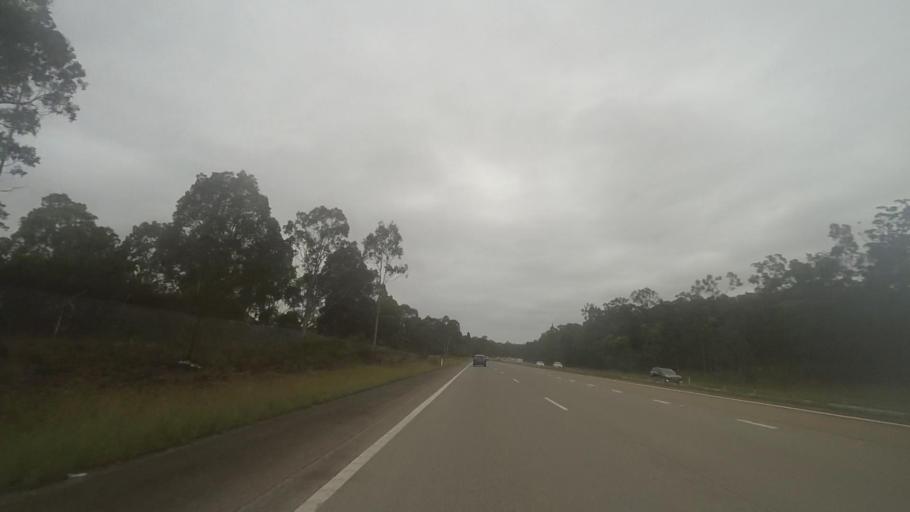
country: AU
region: New South Wales
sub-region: Port Stephens Shire
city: Medowie
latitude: -32.6907
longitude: 151.8091
